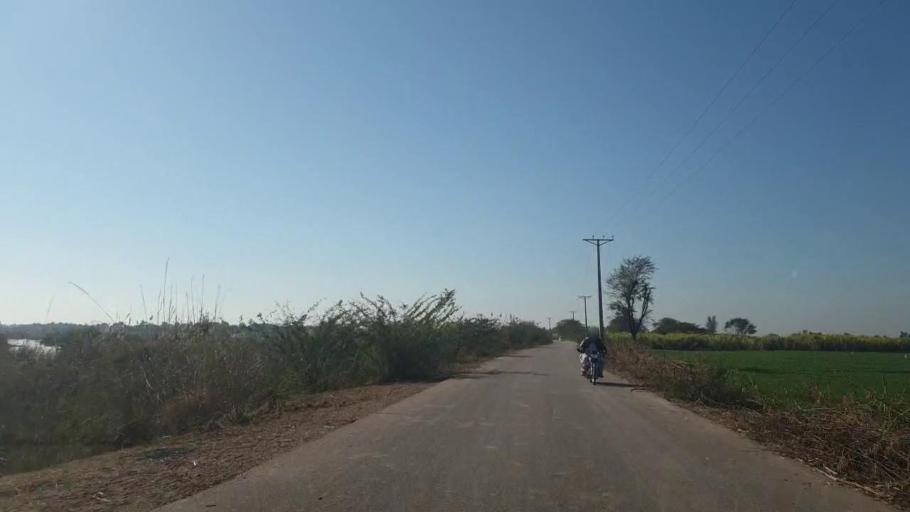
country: PK
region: Sindh
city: Kot Diji
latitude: 27.3014
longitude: 68.6436
